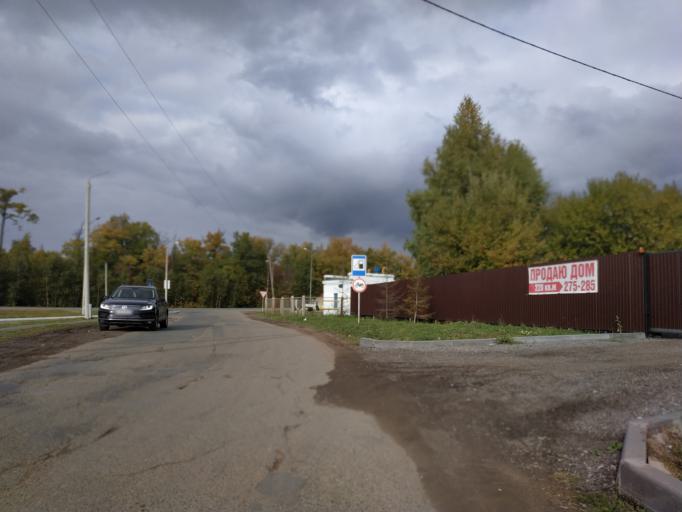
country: RU
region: Chuvashia
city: Ishley
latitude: 56.1330
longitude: 47.0865
